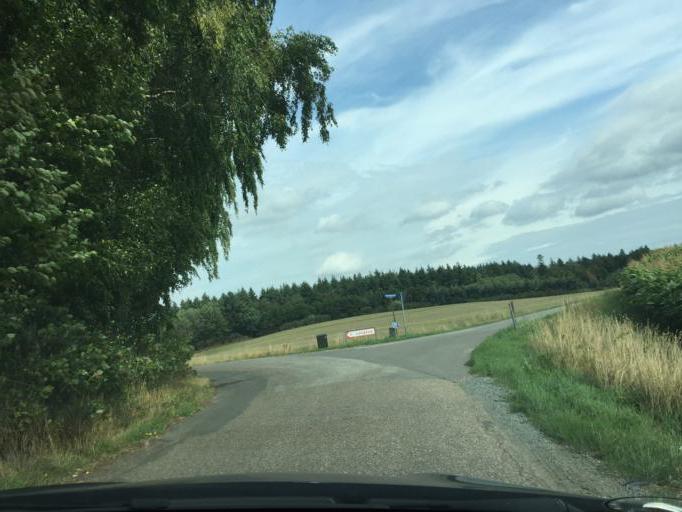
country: DK
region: South Denmark
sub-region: Assens Kommune
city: Vissenbjerg
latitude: 55.4124
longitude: 10.1929
